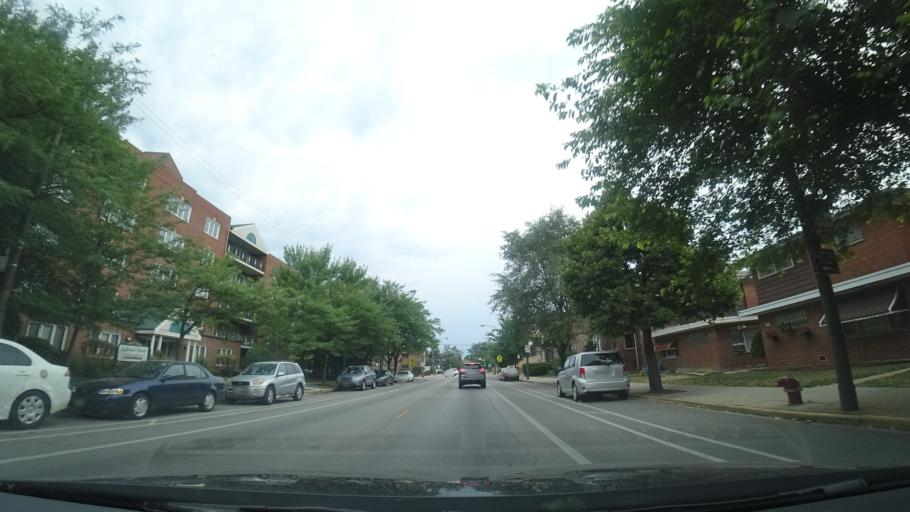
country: US
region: Illinois
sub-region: Cook County
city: Harwood Heights
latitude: 41.9689
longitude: -87.7675
